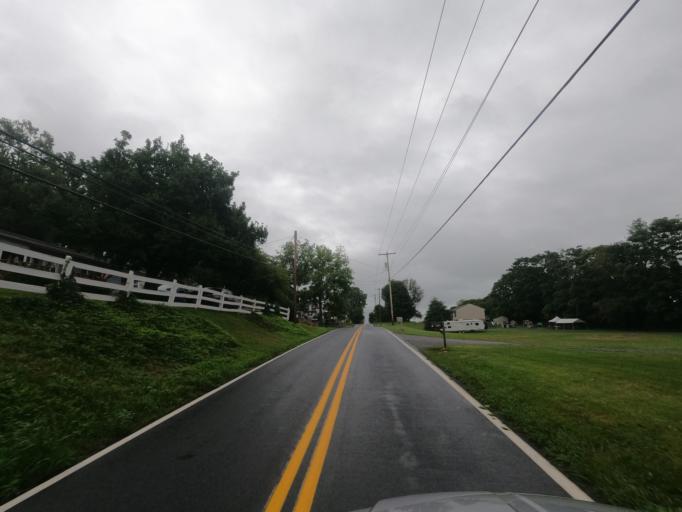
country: US
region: Maryland
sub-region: Washington County
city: Wilson-Conococheague
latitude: 39.6260
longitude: -77.9441
